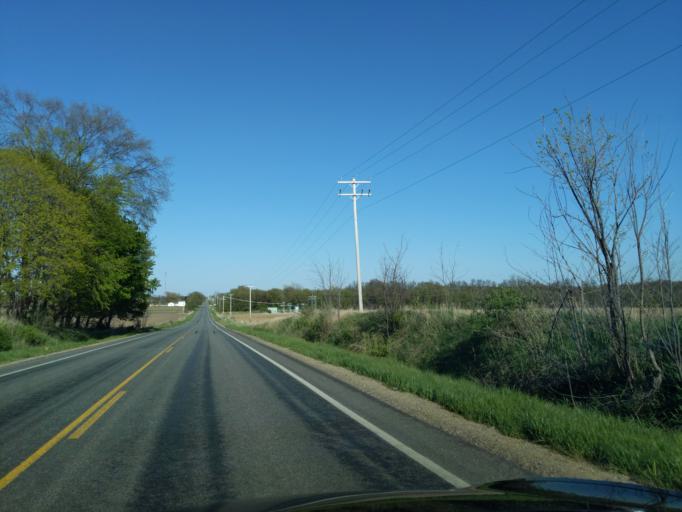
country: US
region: Michigan
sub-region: Ionia County
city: Ionia
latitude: 42.8860
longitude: -85.0718
